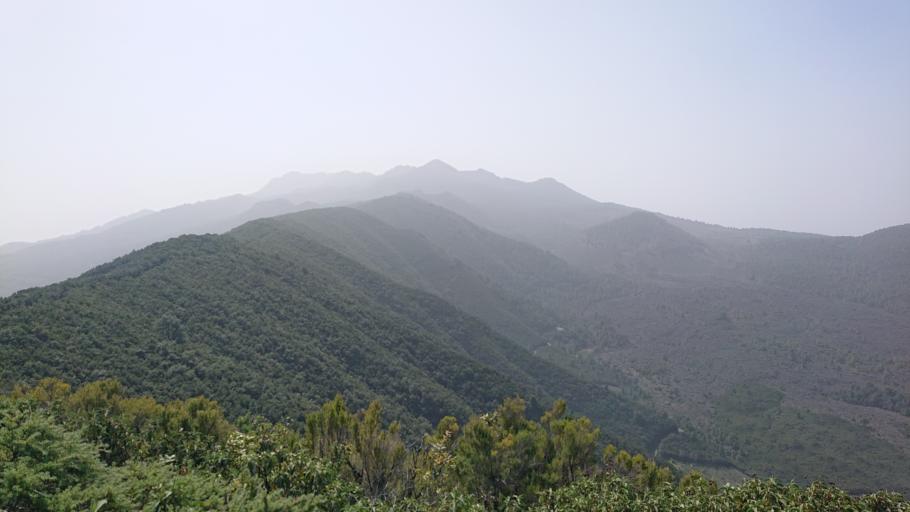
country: ES
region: Canary Islands
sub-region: Provincia de Santa Cruz de Tenerife
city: Brena Baja
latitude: 28.6428
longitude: -17.8254
